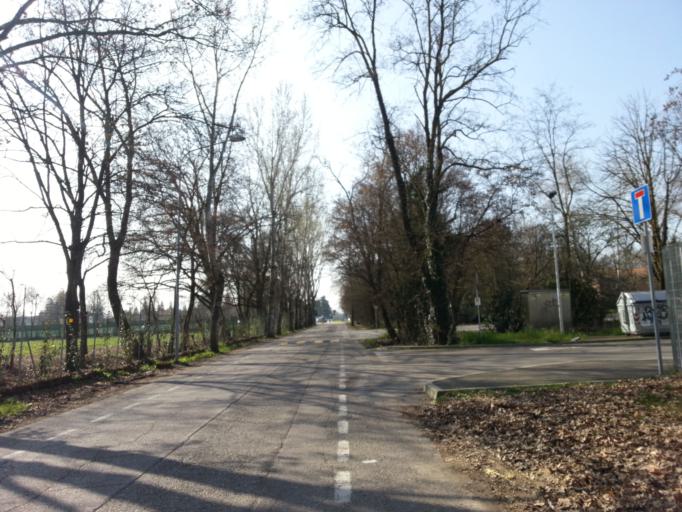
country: IT
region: Emilia-Romagna
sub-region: Provincia di Reggio Emilia
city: Forche
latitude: 44.6644
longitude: 10.5905
